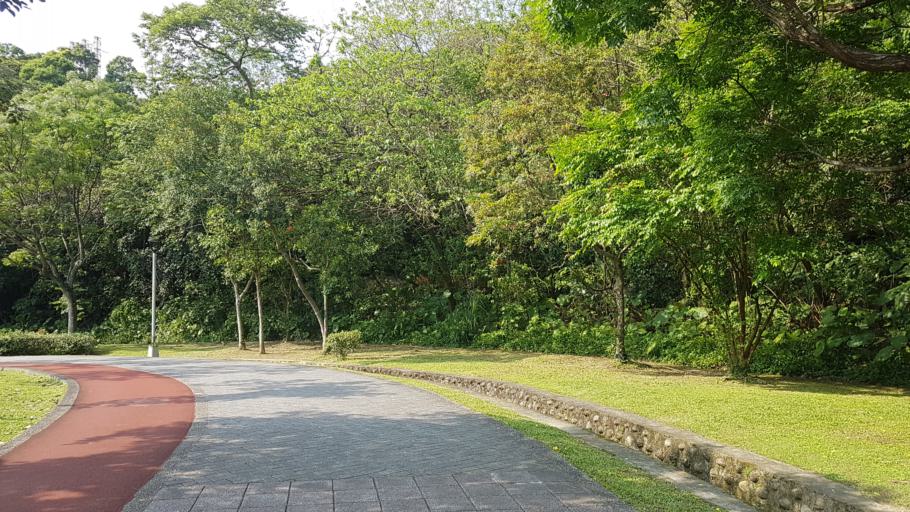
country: TW
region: Taipei
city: Taipei
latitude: 25.0031
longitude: 121.5444
